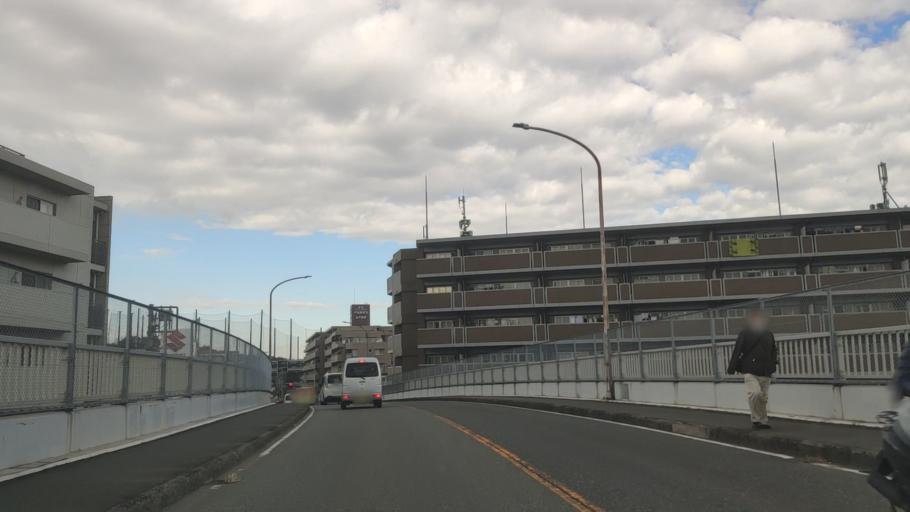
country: JP
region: Kanagawa
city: Fujisawa
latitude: 35.4158
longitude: 139.5411
